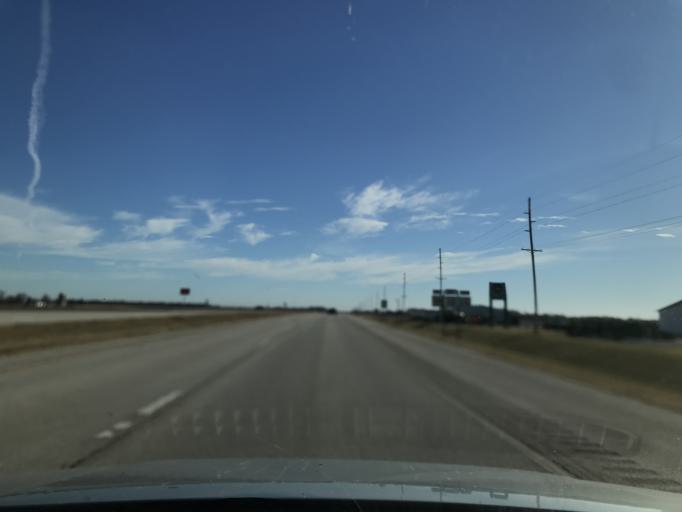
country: US
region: Illinois
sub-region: Hancock County
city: Carthage
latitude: 40.4152
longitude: -91.0629
